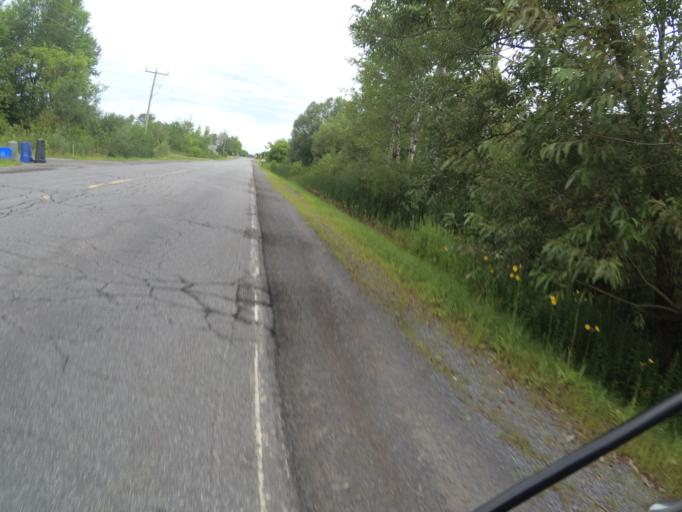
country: CA
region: Ontario
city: Bourget
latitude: 45.3635
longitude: -75.2631
